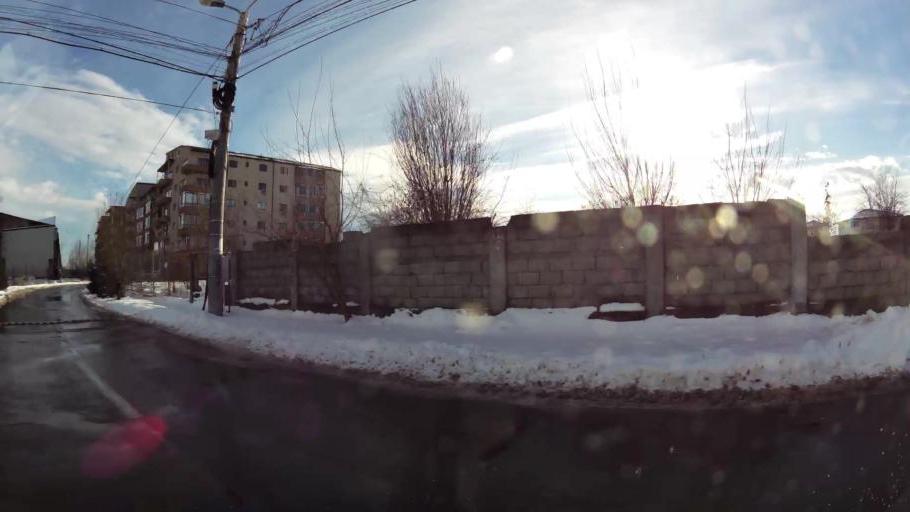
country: RO
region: Ilfov
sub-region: Voluntari City
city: Voluntari
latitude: 44.4911
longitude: 26.2000
